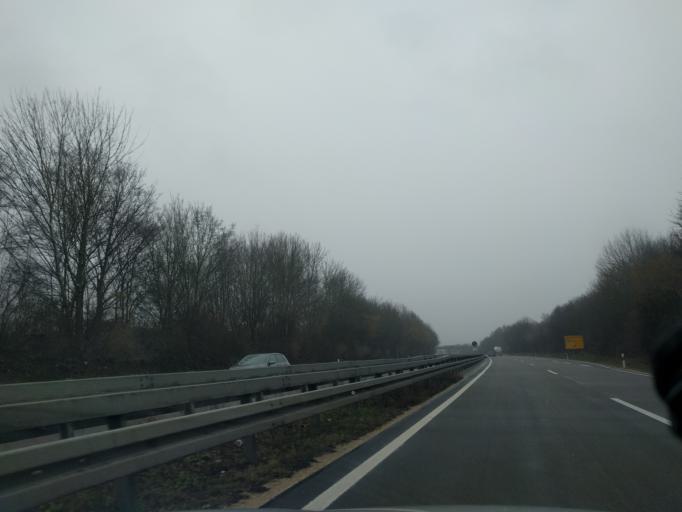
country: DE
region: Bavaria
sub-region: Swabia
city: Asbach-Baumenheim
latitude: 48.6808
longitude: 10.8243
